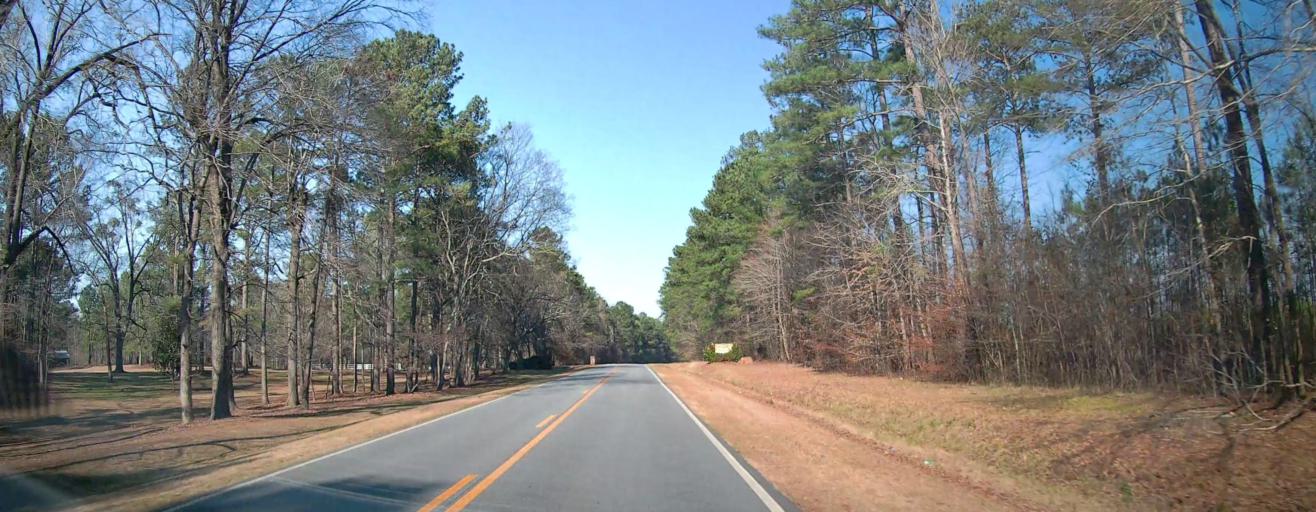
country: US
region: Georgia
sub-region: Monroe County
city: Forsyth
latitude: 33.0934
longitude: -83.8371
